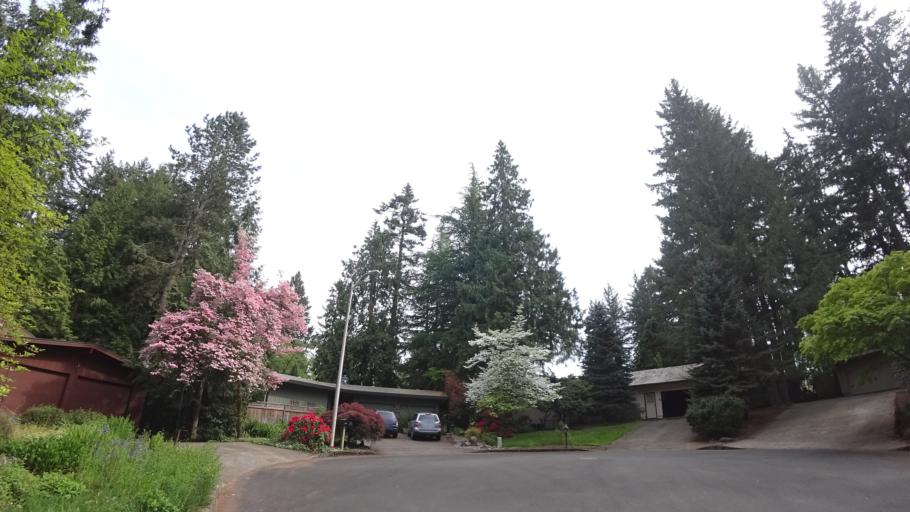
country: US
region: Oregon
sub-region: Washington County
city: Hillsboro
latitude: 45.5088
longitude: -122.9436
